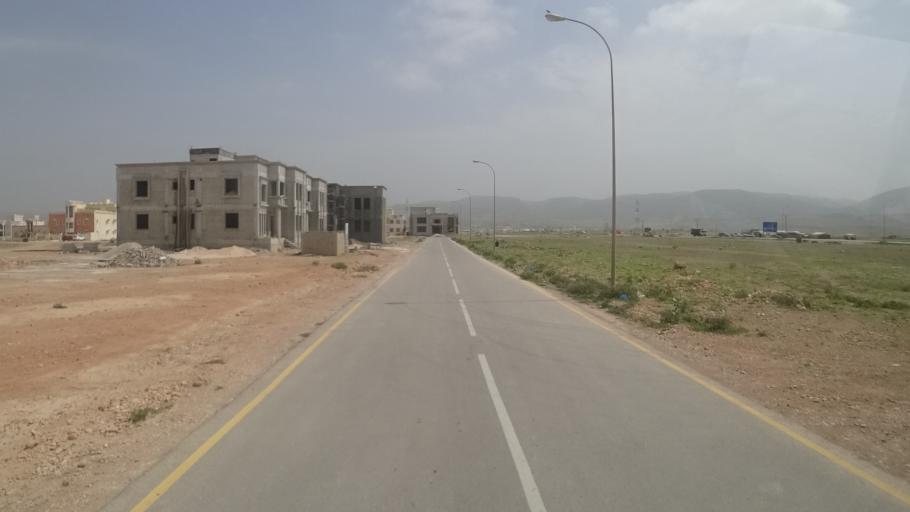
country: OM
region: Zufar
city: Salalah
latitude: 17.0980
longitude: 54.2157
